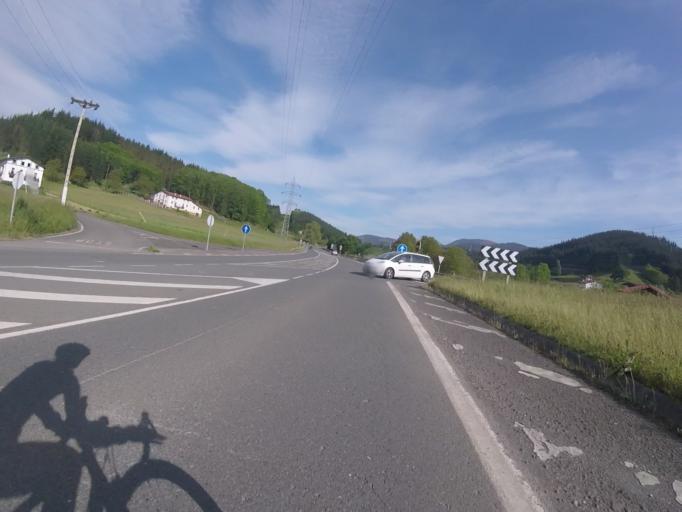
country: ES
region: Basque Country
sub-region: Provincia de Guipuzcoa
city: Ormaiztegui
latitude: 43.0527
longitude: -2.2631
